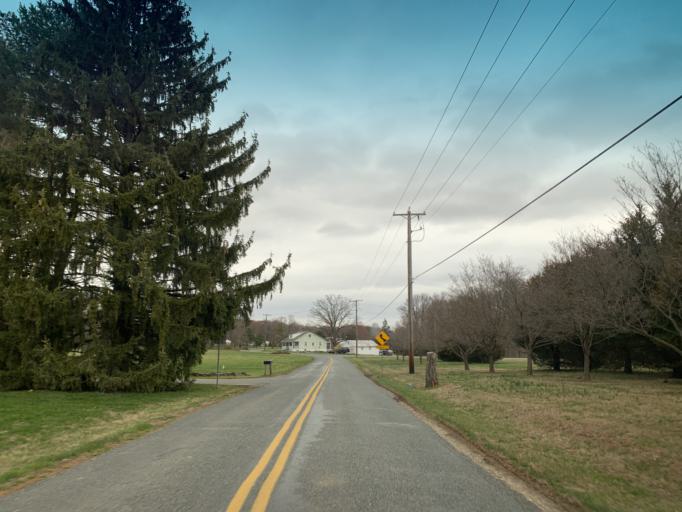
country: US
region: Maryland
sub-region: Harford County
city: Aberdeen
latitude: 39.5524
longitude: -76.1948
